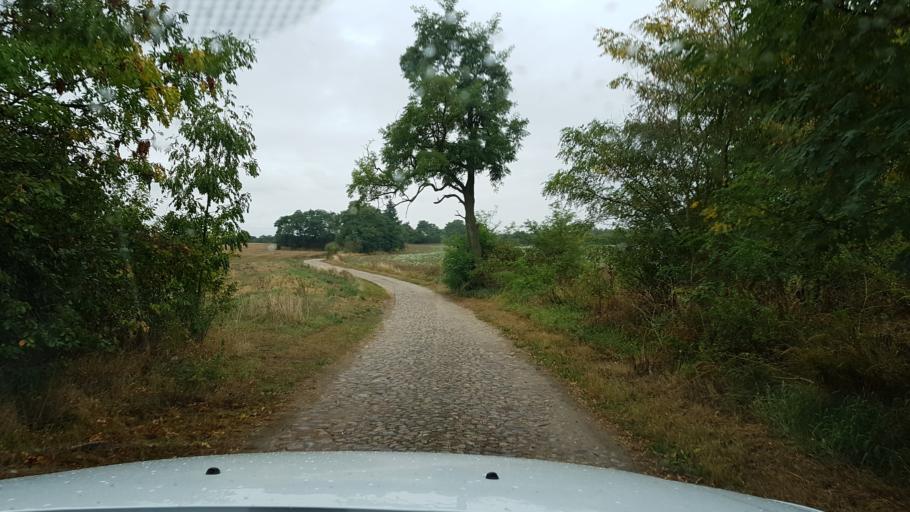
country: PL
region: West Pomeranian Voivodeship
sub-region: Powiat gryfinski
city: Cedynia
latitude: 52.8505
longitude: 14.2900
